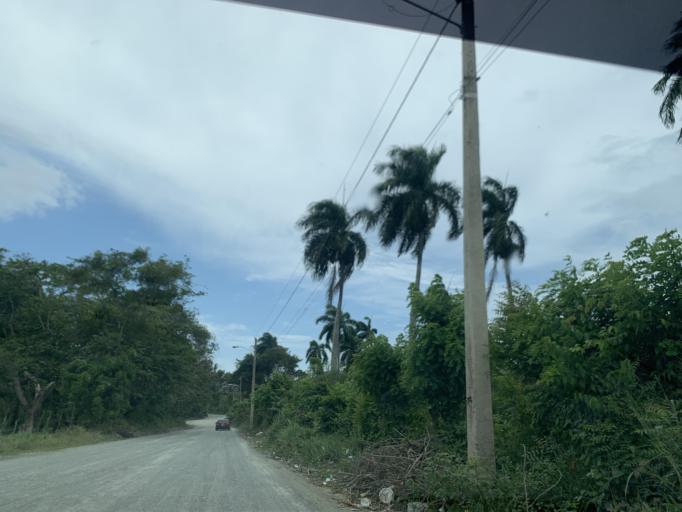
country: DO
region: Puerto Plata
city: Imbert
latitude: 19.8191
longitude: -70.7791
